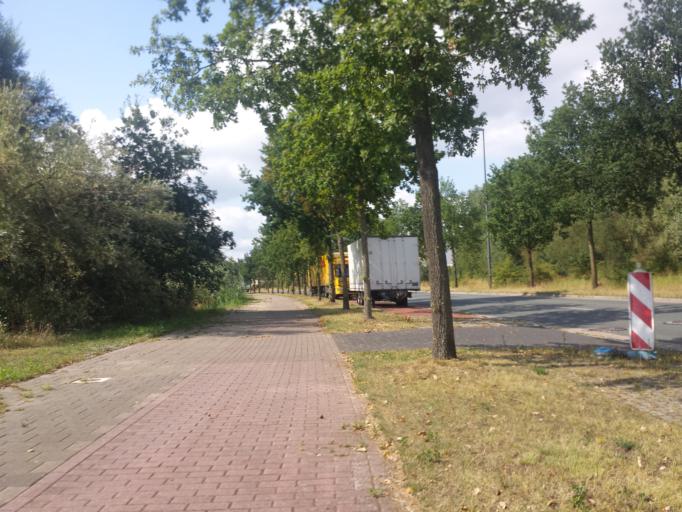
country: DE
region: Lower Saxony
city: Stuhr
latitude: 53.0955
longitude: 8.7095
